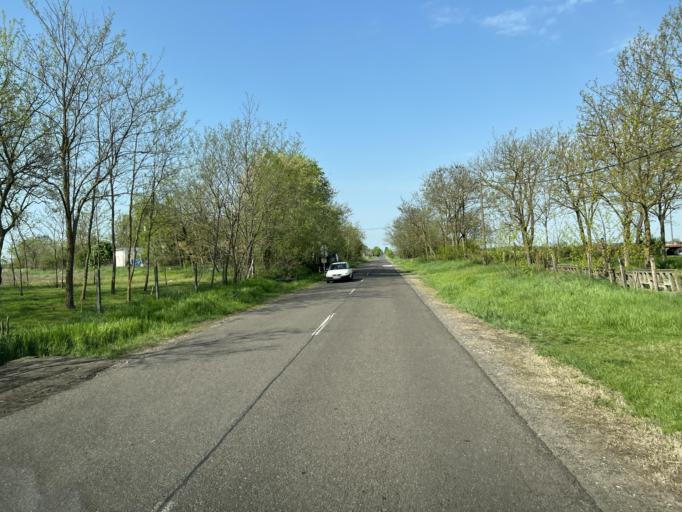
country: HU
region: Pest
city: Jaszkarajeno
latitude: 47.0449
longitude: 20.0674
